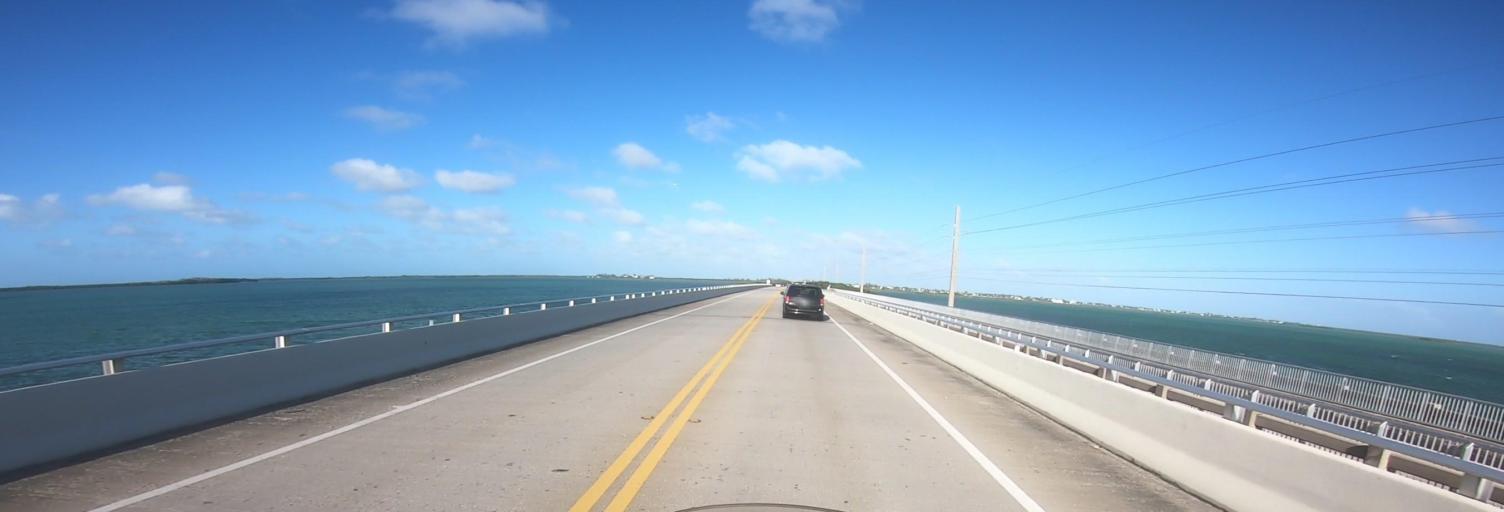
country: US
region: Florida
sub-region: Monroe County
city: Big Coppitt Key
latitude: 24.6330
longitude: -81.5866
